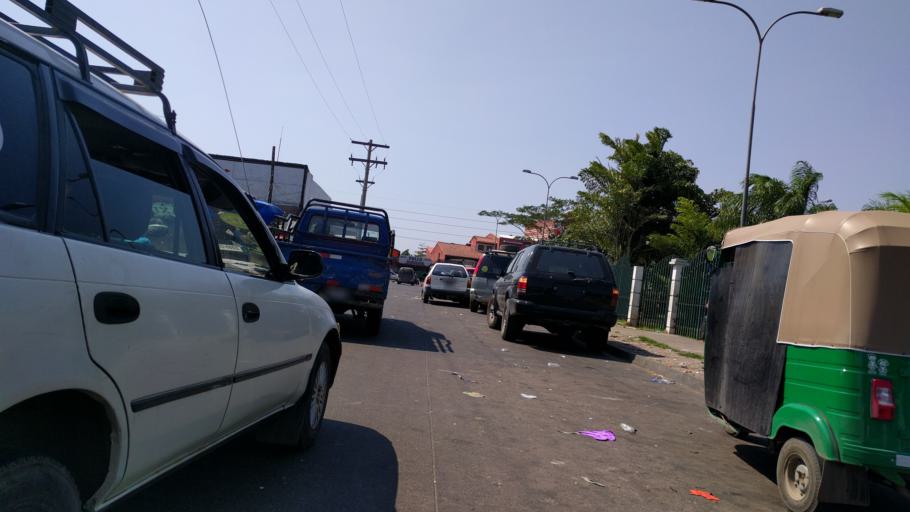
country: BO
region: Santa Cruz
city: Santa Cruz de la Sierra
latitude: -17.7981
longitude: -63.2046
